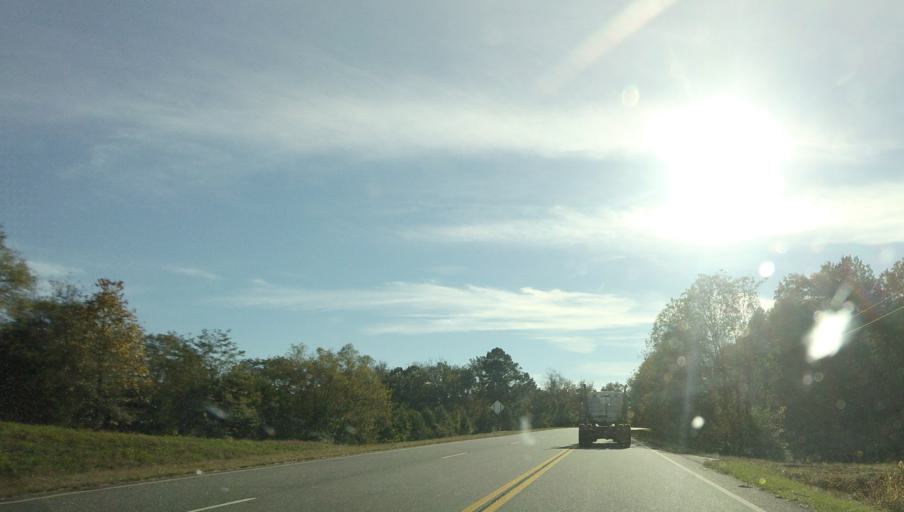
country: US
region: Georgia
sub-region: Talbot County
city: Talbotton
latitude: 32.7006
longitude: -84.4151
